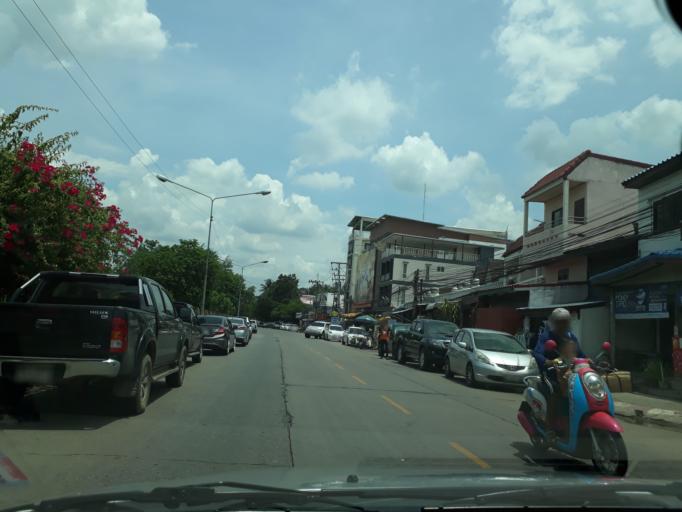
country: TH
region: Khon Kaen
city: Khon Kaen
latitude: 16.4116
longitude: 102.8351
